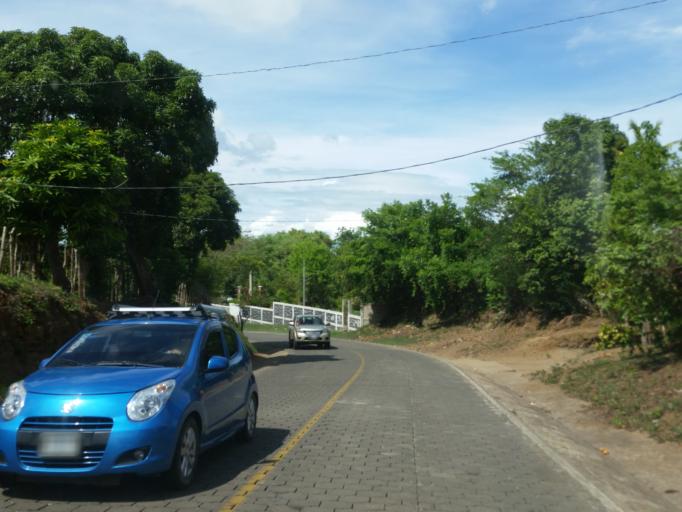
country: NI
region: Masaya
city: Masaya
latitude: 11.9679
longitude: -86.0321
